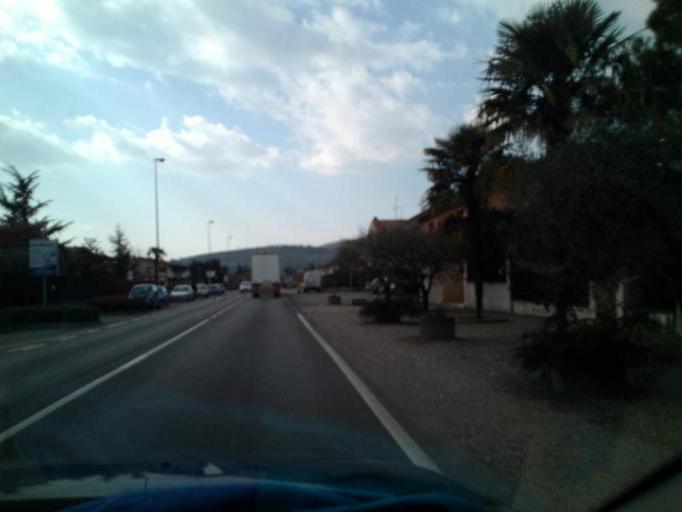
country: IT
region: Veneto
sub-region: Provincia di Verona
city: San Pietro in Cariano
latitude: 45.5217
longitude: 10.8834
